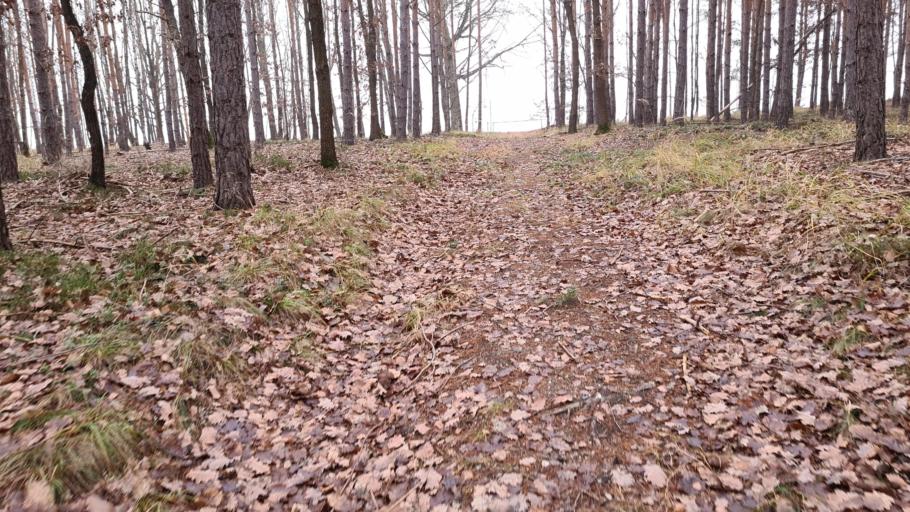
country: DE
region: Brandenburg
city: Plessa
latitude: 51.5280
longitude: 13.6760
